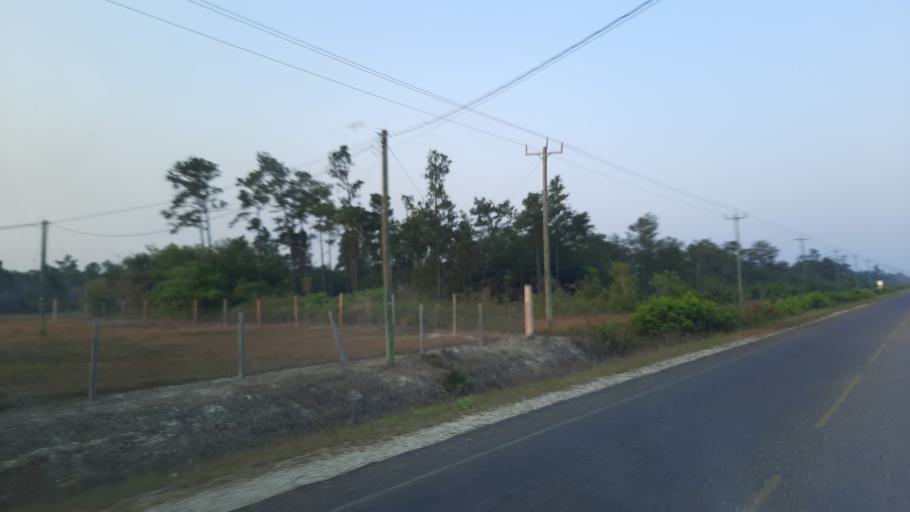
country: BZ
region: Stann Creek
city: Placencia
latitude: 16.5319
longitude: -88.4461
